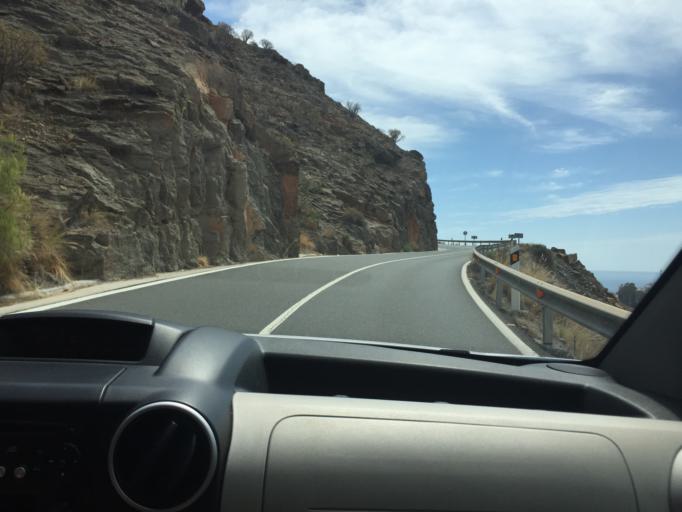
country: ES
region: Canary Islands
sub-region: Provincia de Las Palmas
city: Puerto Rico
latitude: 27.8242
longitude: -15.7573
